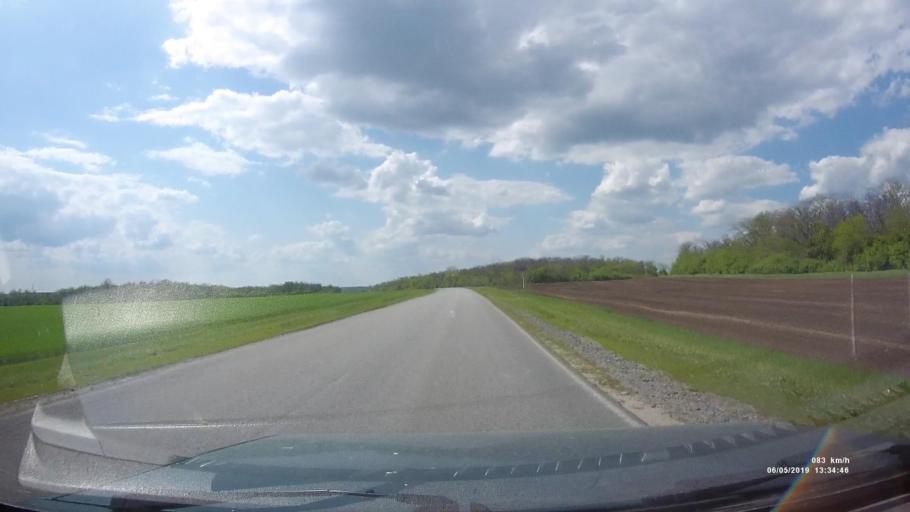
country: RU
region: Rostov
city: Ust'-Donetskiy
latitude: 47.6937
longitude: 40.7575
